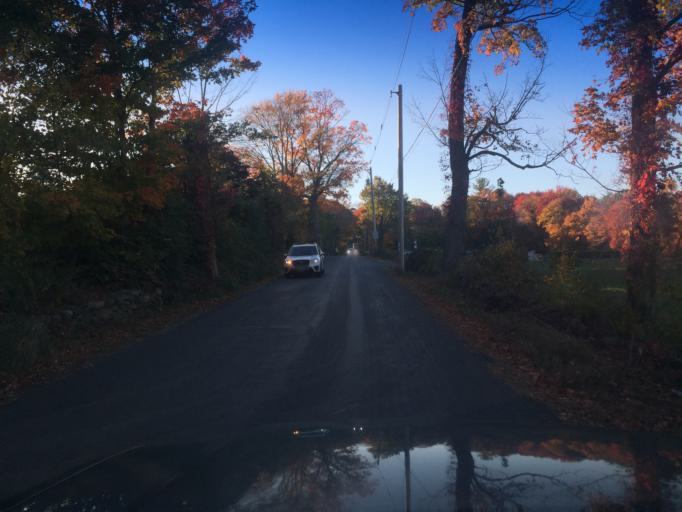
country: US
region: Massachusetts
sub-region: Middlesex County
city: Stow
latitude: 42.4117
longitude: -71.5139
